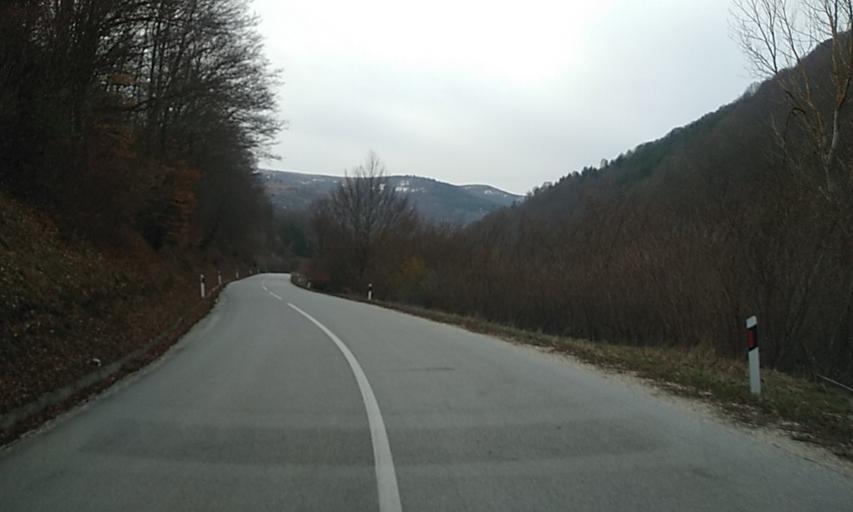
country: RS
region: Central Serbia
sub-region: Pcinjski Okrug
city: Bosilegrad
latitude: 42.5969
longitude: 22.4100
